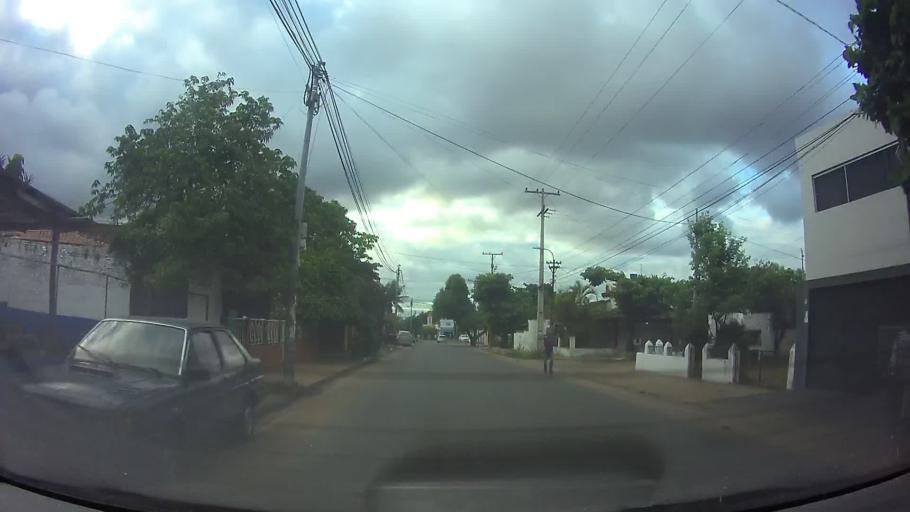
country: PY
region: Central
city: Fernando de la Mora
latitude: -25.3163
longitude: -57.5461
